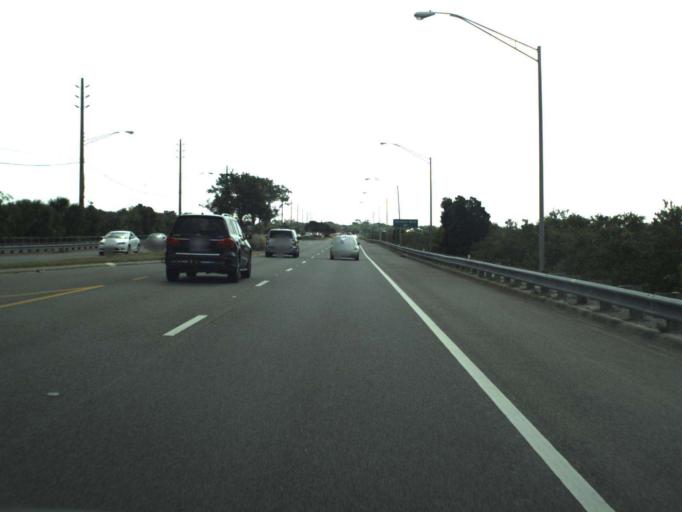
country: US
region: Florida
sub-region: Volusia County
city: New Smyrna Beach
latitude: 29.0263
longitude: -80.9107
